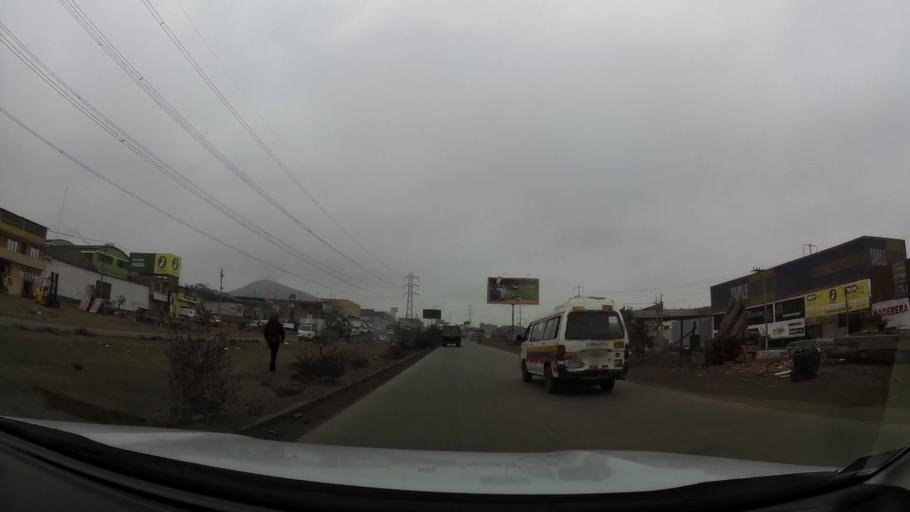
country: PE
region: Lima
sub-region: Lima
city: Surco
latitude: -12.2009
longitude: -76.9315
